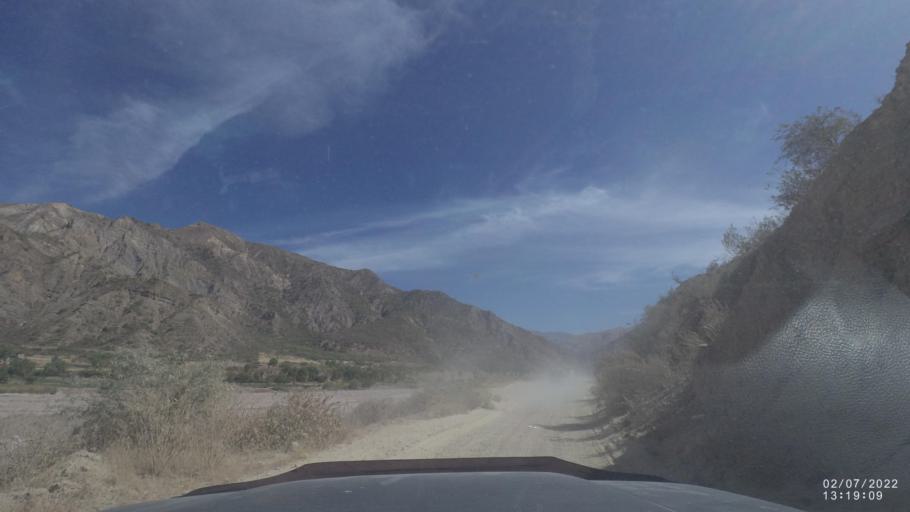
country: BO
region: Cochabamba
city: Irpa Irpa
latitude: -17.7338
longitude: -66.3145
